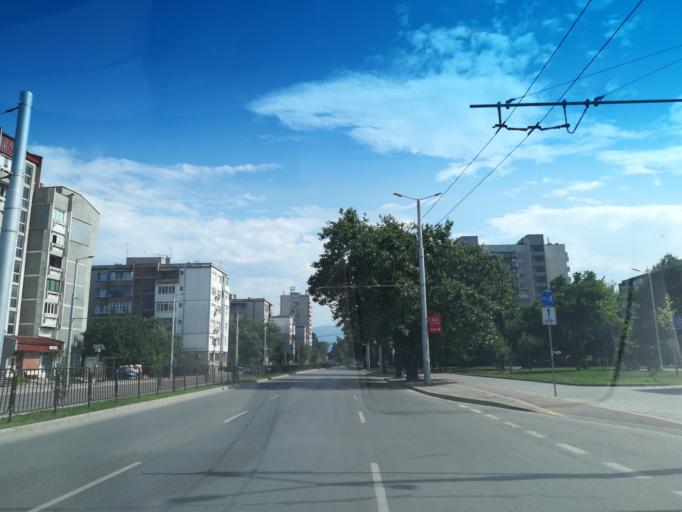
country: BG
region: Plovdiv
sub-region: Obshtina Plovdiv
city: Plovdiv
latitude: 42.1463
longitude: 24.7631
